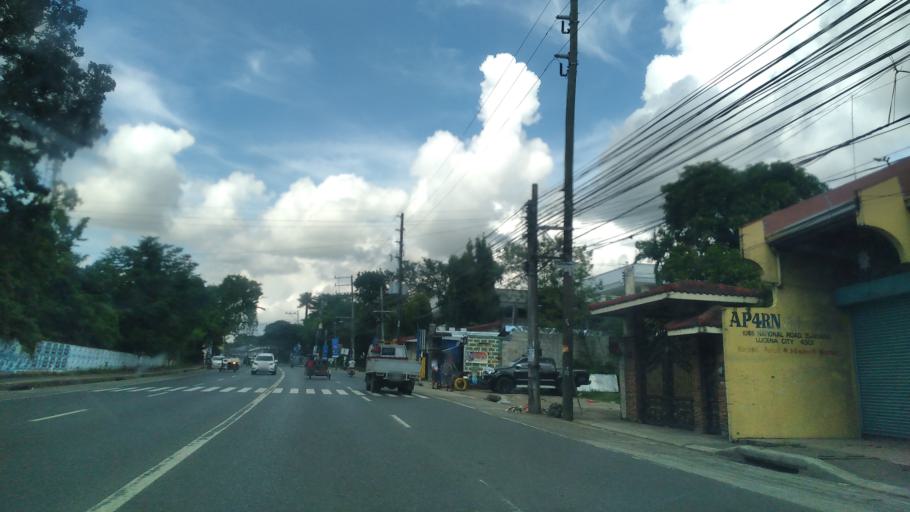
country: PH
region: Calabarzon
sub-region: Province of Quezon
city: Isabang
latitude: 13.9457
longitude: 121.5903
